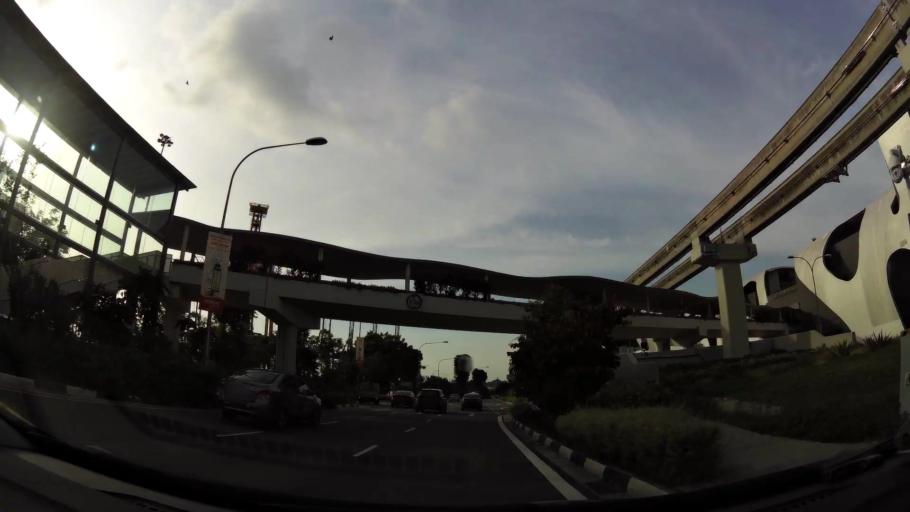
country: SG
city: Singapore
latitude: 1.2647
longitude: 103.8240
